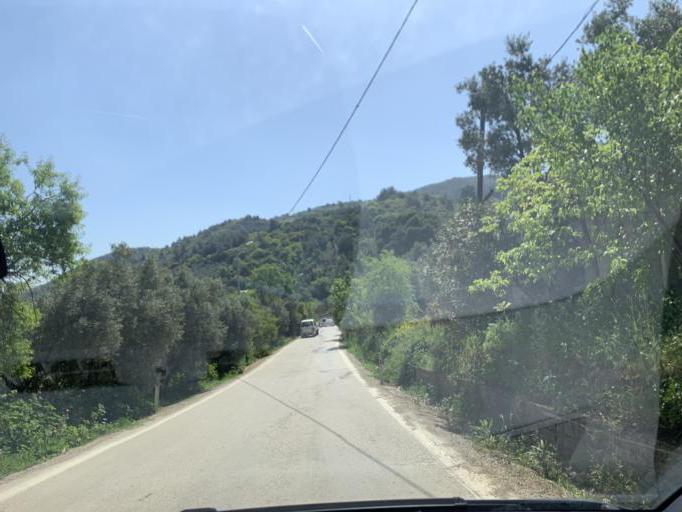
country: TR
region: Bursa
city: Niluefer
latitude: 40.3537
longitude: 28.9661
